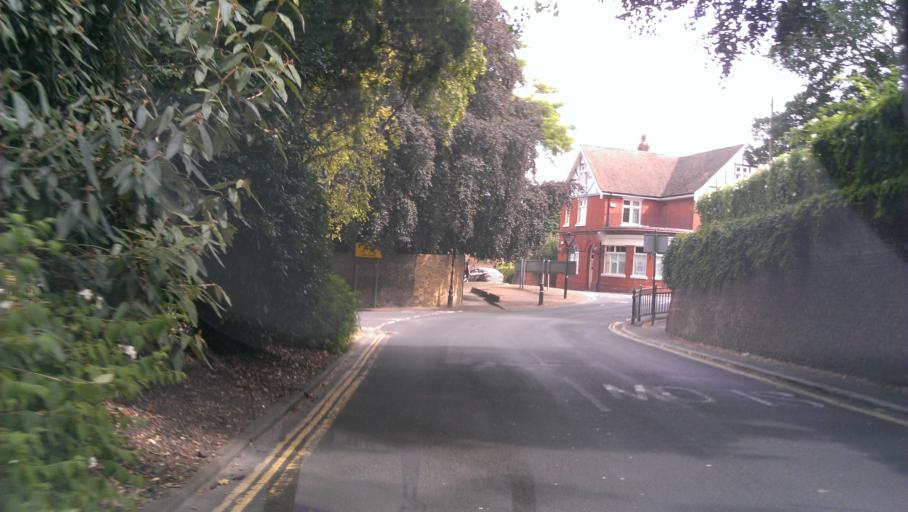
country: GB
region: England
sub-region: Medway
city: Rochester
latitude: 51.3860
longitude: 0.5034
